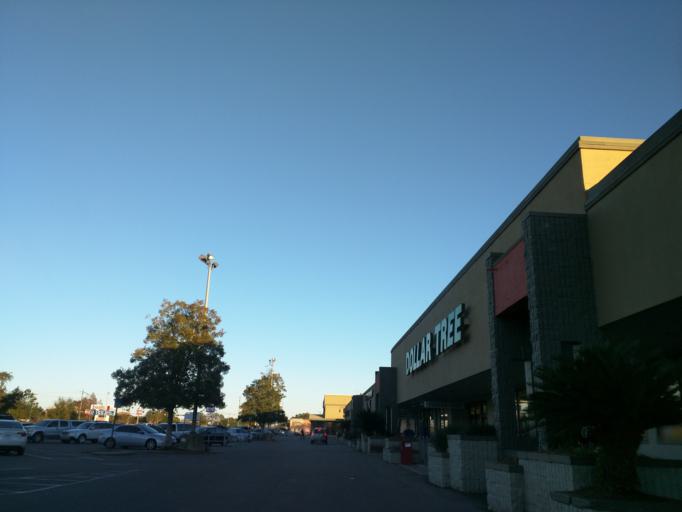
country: US
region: Florida
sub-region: Leon County
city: Tallahassee
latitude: 30.4367
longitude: -84.2646
